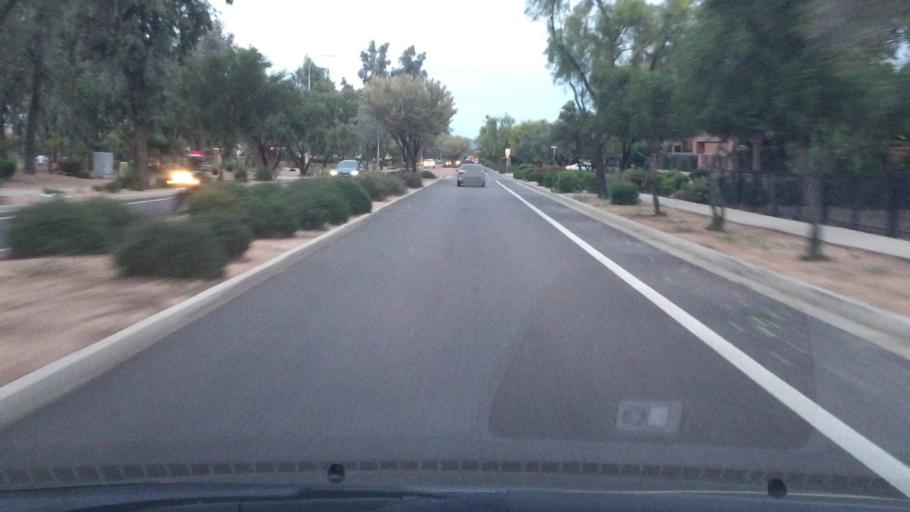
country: US
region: Arizona
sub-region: Maricopa County
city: Guadalupe
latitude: 33.3810
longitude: -112.0127
